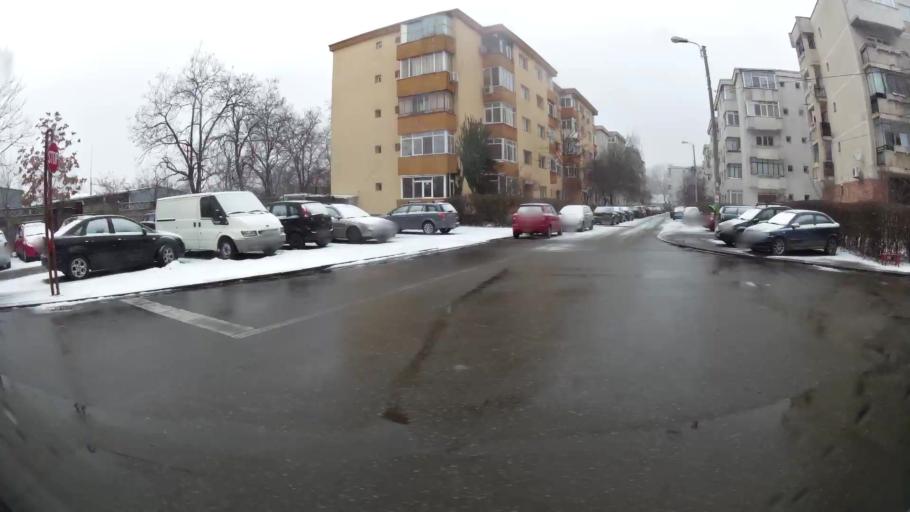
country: RO
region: Prahova
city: Ploiesti
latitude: 44.9361
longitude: 25.9980
